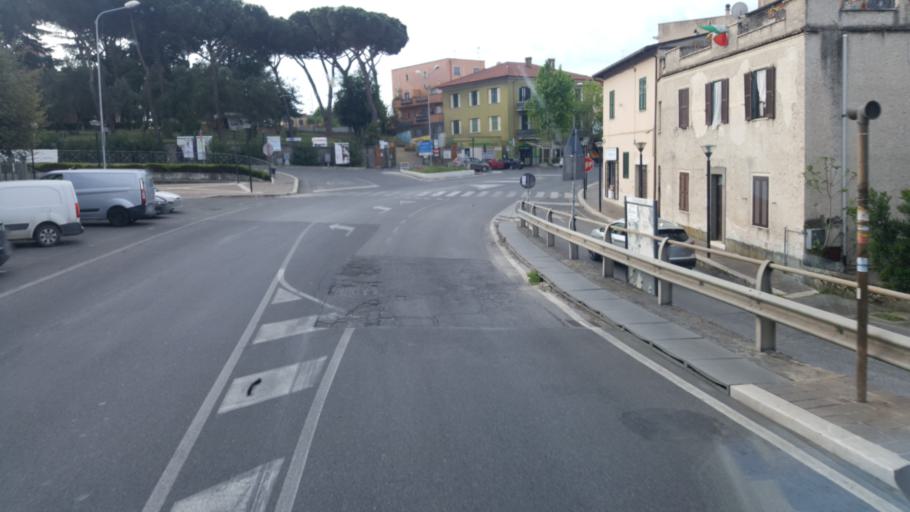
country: IT
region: Latium
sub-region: Citta metropolitana di Roma Capitale
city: Cecchina
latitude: 41.6973
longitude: 12.6494
